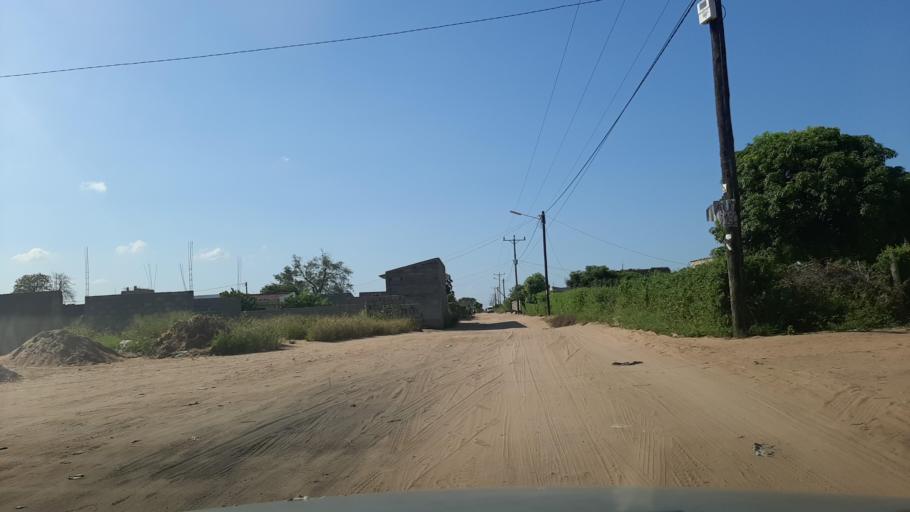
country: MZ
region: Maputo
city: Matola
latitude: -25.8048
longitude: 32.4910
